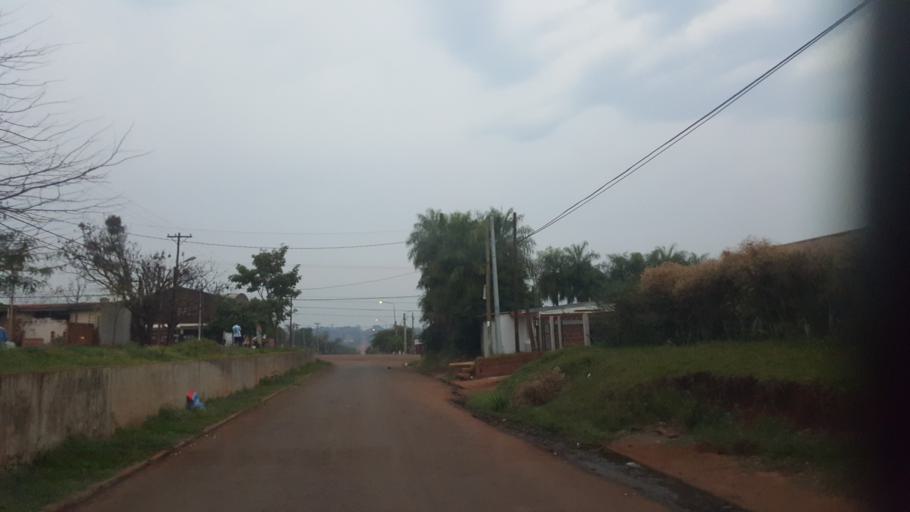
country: AR
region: Misiones
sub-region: Departamento de Capital
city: Posadas
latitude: -27.3861
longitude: -55.9382
